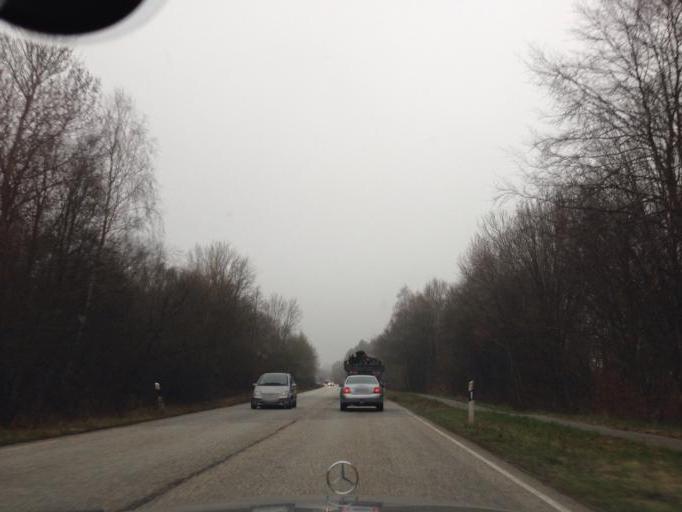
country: DE
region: Schleswig-Holstein
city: Klein Barkau
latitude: 54.2559
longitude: 10.1483
